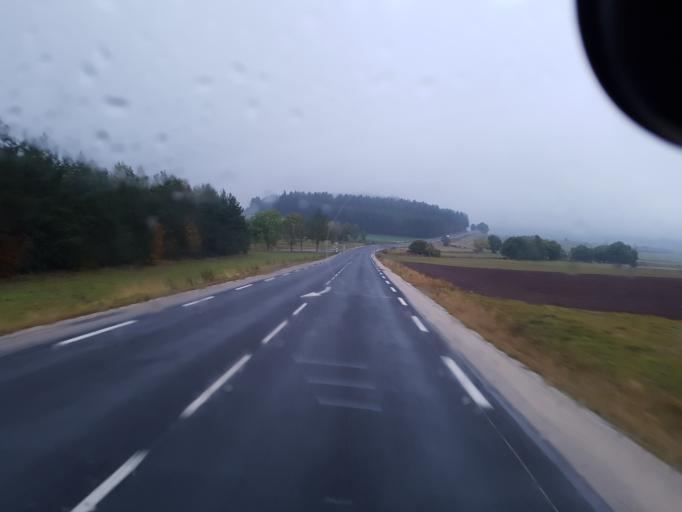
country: FR
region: Languedoc-Roussillon
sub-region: Departement de la Lozere
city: Langogne
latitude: 44.8262
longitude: 3.8706
